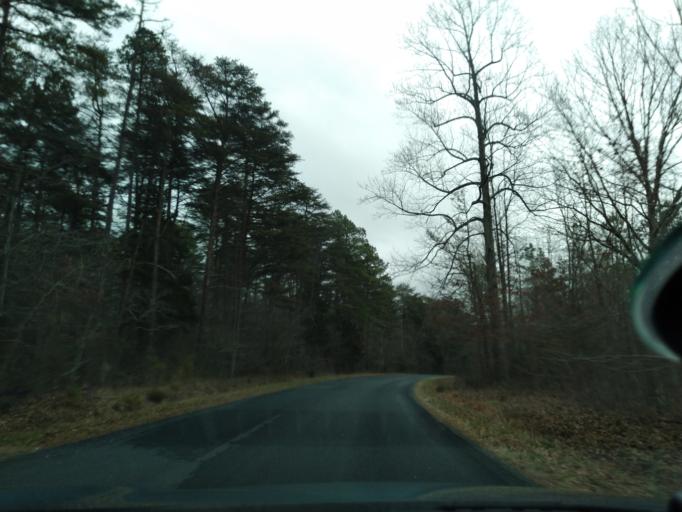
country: US
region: Virginia
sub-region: Appomattox County
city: Appomattox
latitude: 37.4124
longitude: -78.6744
